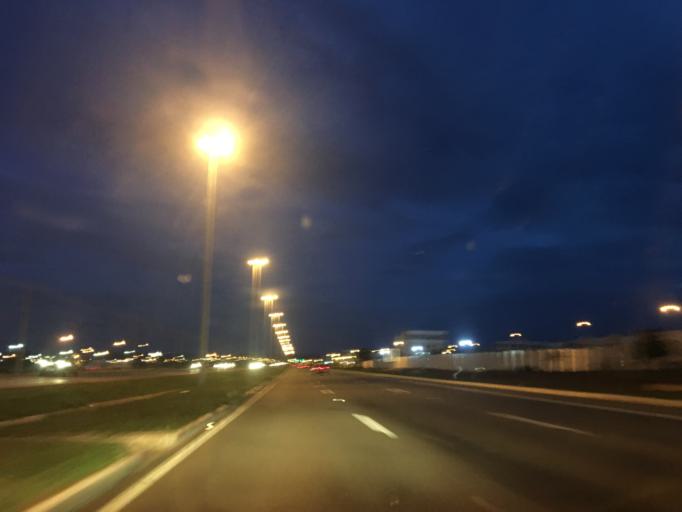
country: BR
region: Federal District
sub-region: Brasilia
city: Brasilia
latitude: -15.8863
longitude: -47.8130
